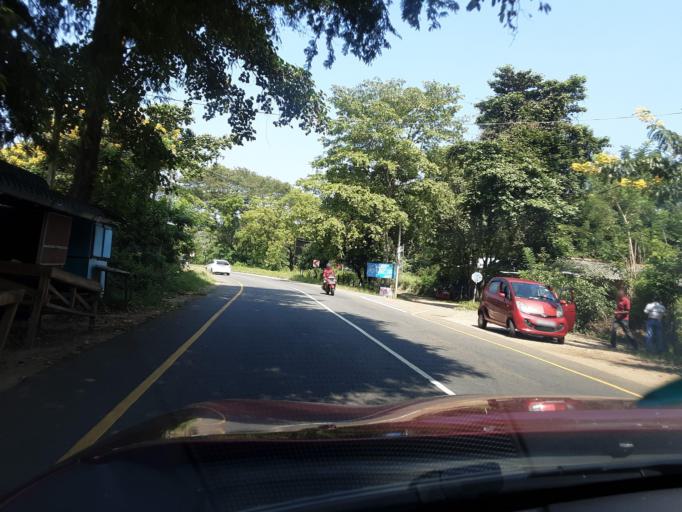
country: LK
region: Uva
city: Badulla
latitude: 7.2864
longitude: 81.0402
